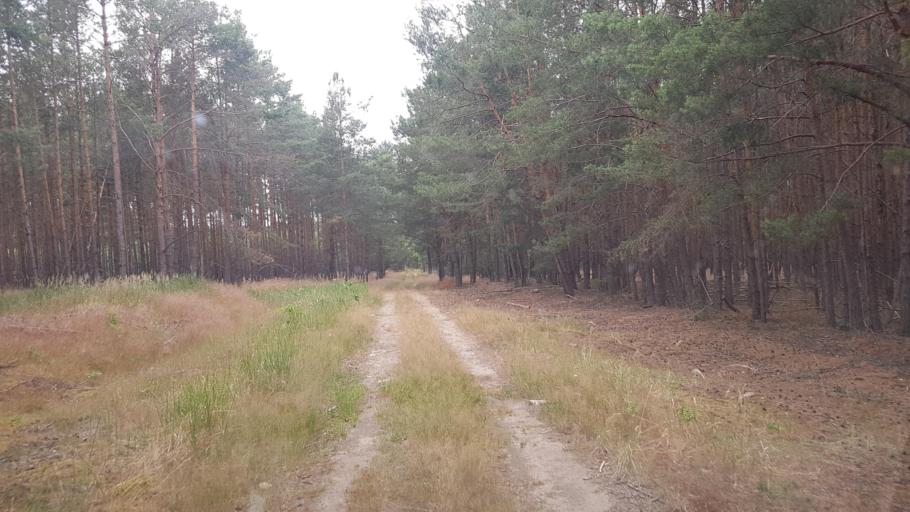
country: DE
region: Brandenburg
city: Treuenbrietzen
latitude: 52.0420
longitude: 12.8289
